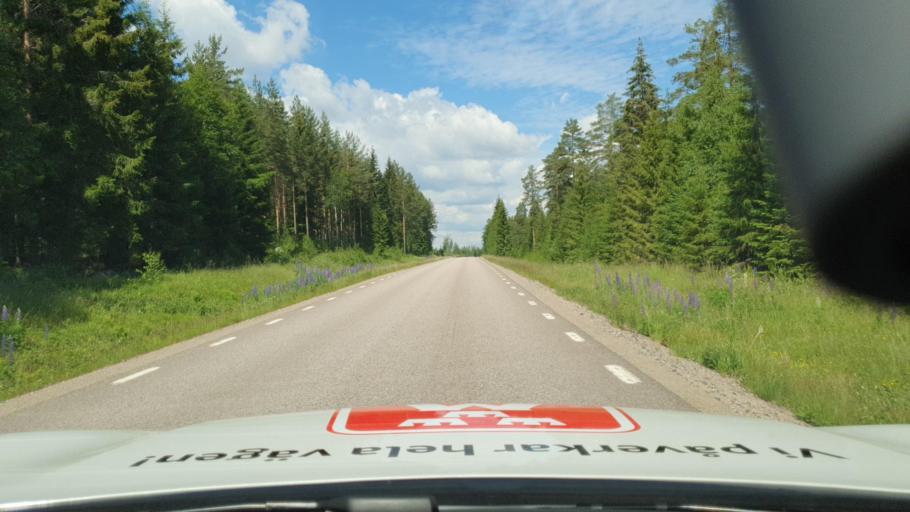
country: SE
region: Vaermland
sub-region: Torsby Kommun
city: Torsby
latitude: 60.4194
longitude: 12.9056
